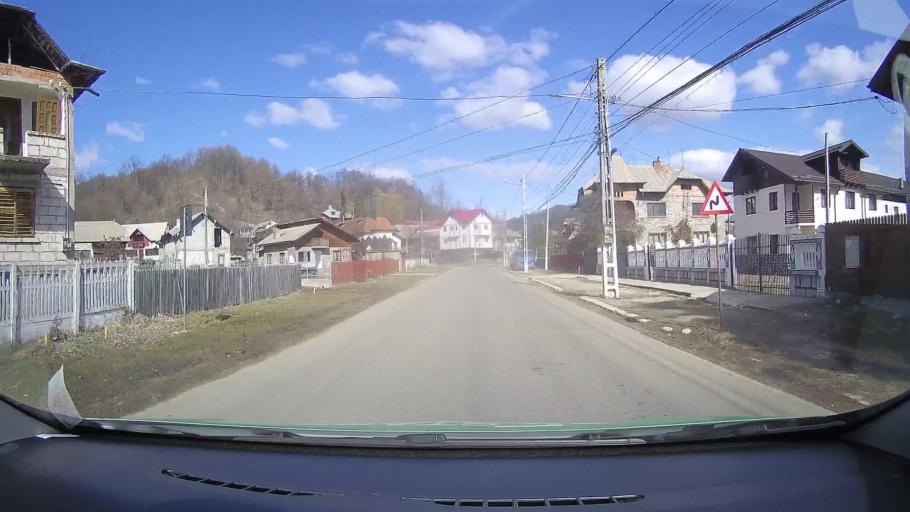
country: RO
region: Dambovita
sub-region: Comuna Vulcana Bai
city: Vulcana Bai
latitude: 45.0741
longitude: 25.3789
